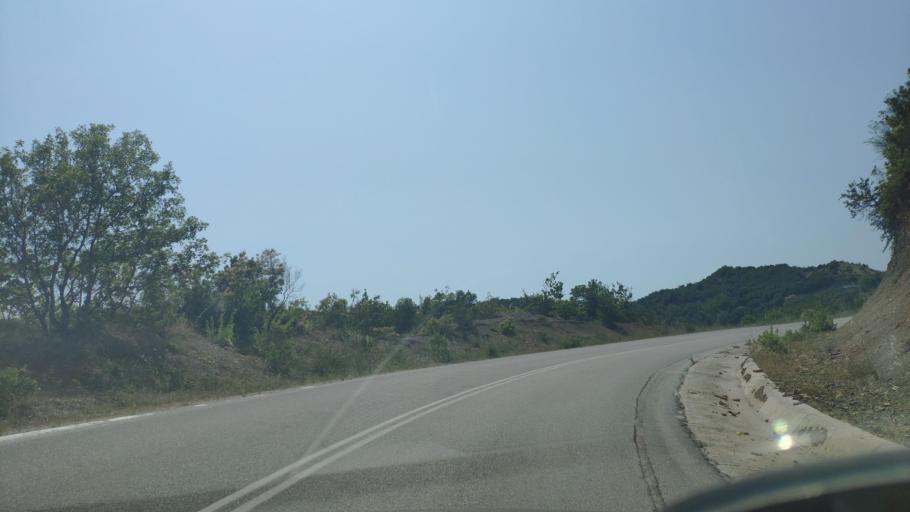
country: GR
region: Epirus
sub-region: Nomos Artas
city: Ano Kalentini
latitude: 39.2184
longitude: 21.1448
